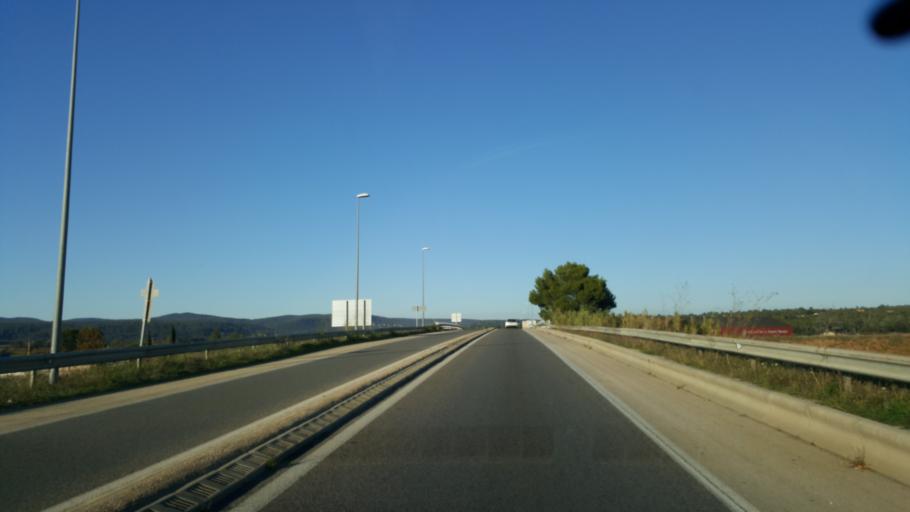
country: FR
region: Provence-Alpes-Cote d'Azur
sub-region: Departement du Var
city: Saint-Maximin-la-Sainte-Baume
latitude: 43.4597
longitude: 5.8634
